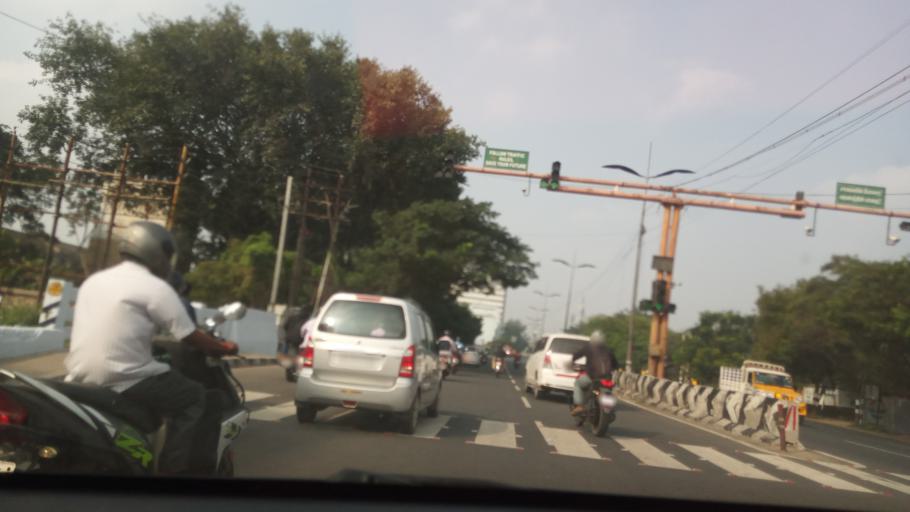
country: IN
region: Tamil Nadu
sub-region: Coimbatore
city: Singanallur
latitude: 11.0249
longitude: 77.0102
